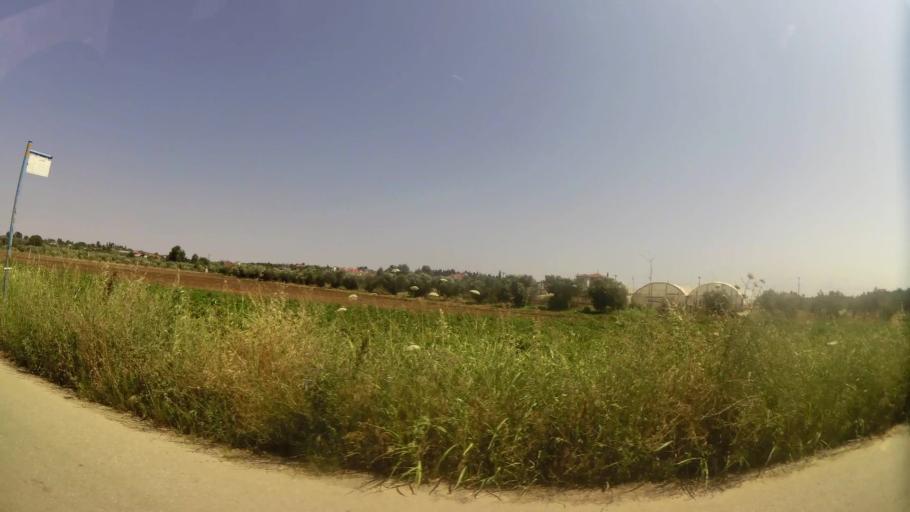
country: GR
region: Central Macedonia
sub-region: Nomos Thessalonikis
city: Nea Michaniona
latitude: 40.4915
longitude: 22.8291
